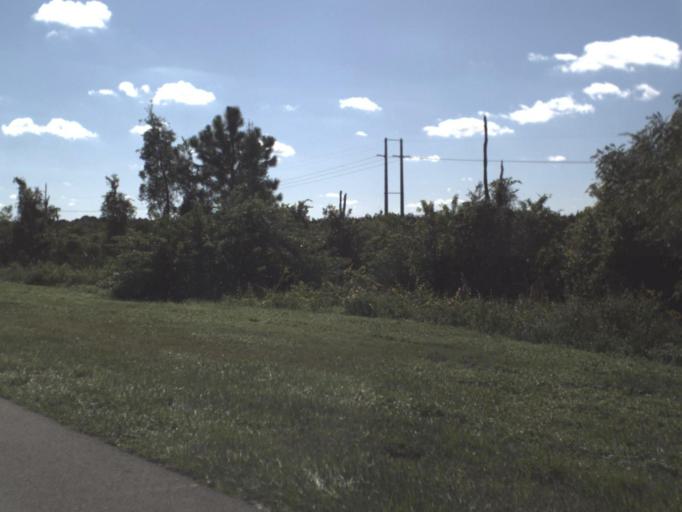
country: US
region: Florida
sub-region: Lee County
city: Lehigh Acres
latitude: 26.5237
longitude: -81.5843
